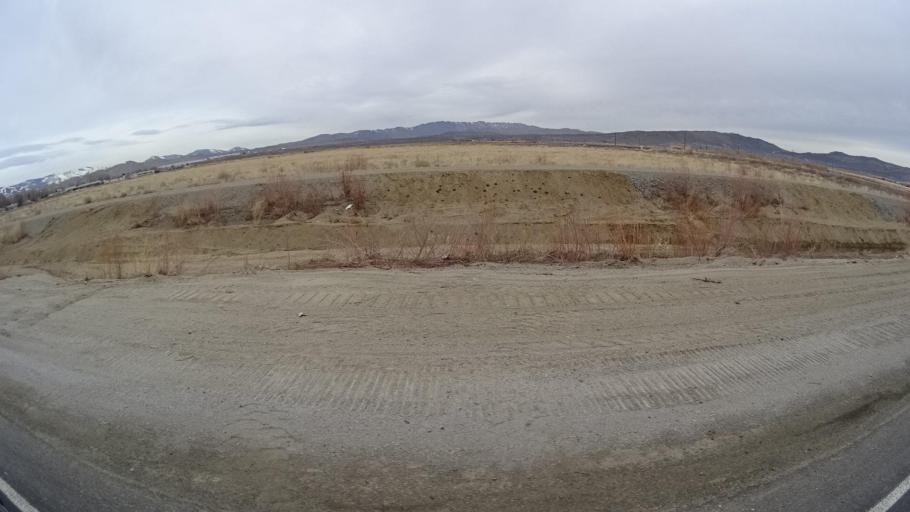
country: US
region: Nevada
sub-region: Washoe County
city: Lemmon Valley
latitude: 39.6459
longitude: -119.8320
